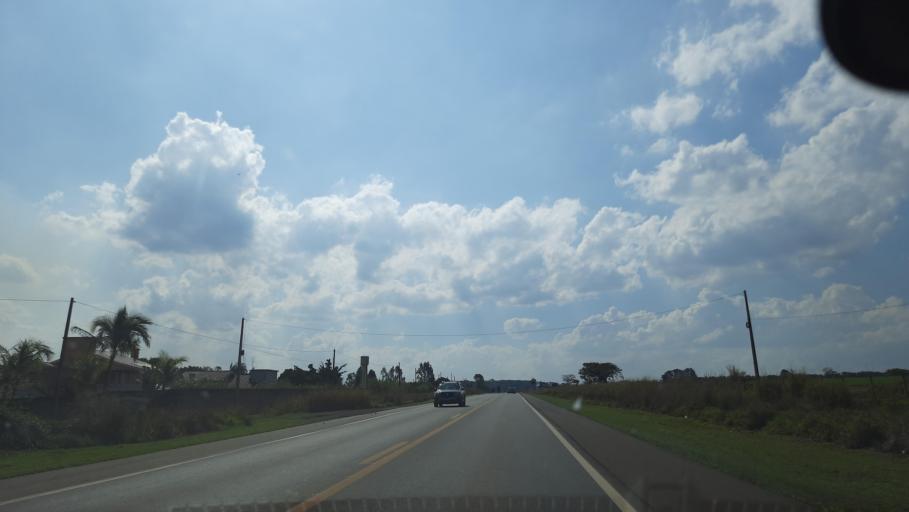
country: BR
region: Sao Paulo
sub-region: Casa Branca
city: Casa Branca
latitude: -21.7800
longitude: -47.0533
